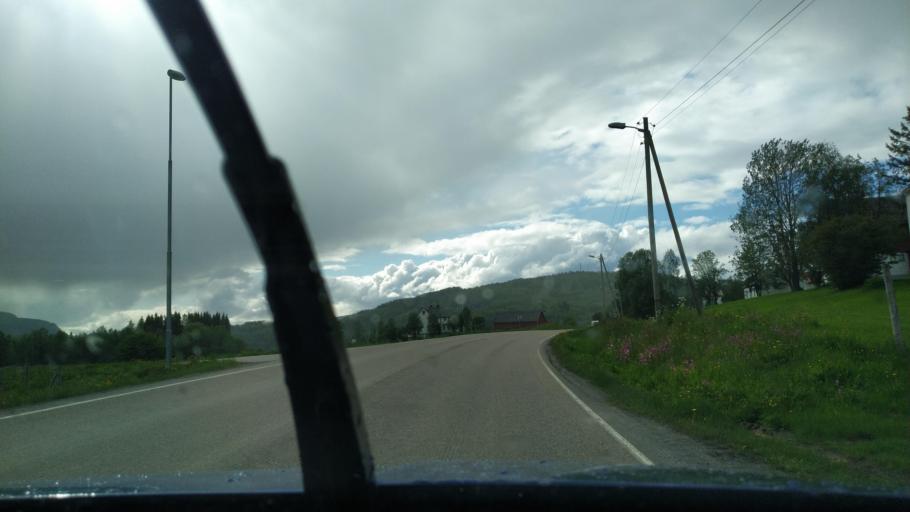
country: NO
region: Troms
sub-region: Sorreisa
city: Sorreisa
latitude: 69.1604
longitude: 18.1260
